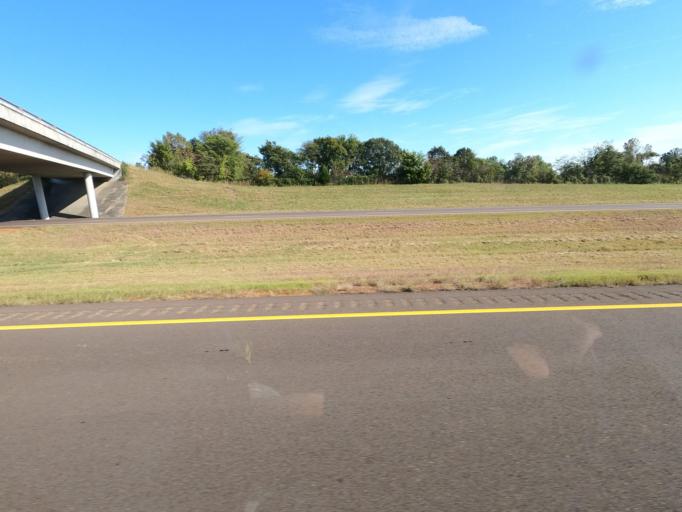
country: US
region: Tennessee
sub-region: Obion County
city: Obion
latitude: 36.3006
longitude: -89.1952
